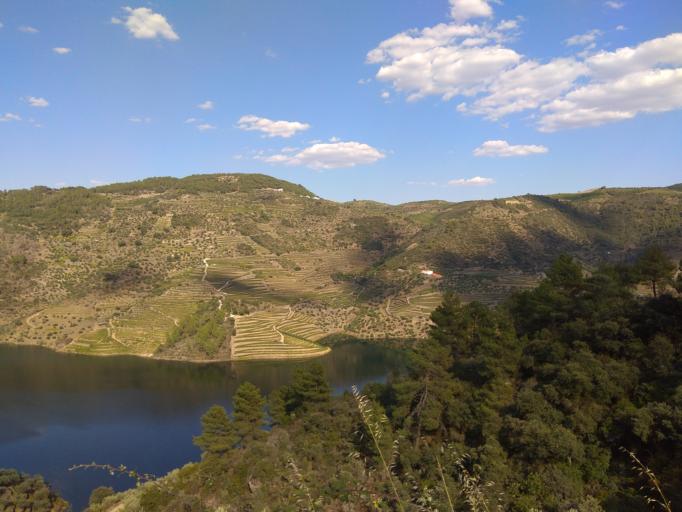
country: PT
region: Viseu
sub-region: Sao Joao da Pesqueira
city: Sao Joao da Pesqueira
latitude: 41.2319
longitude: -7.4289
